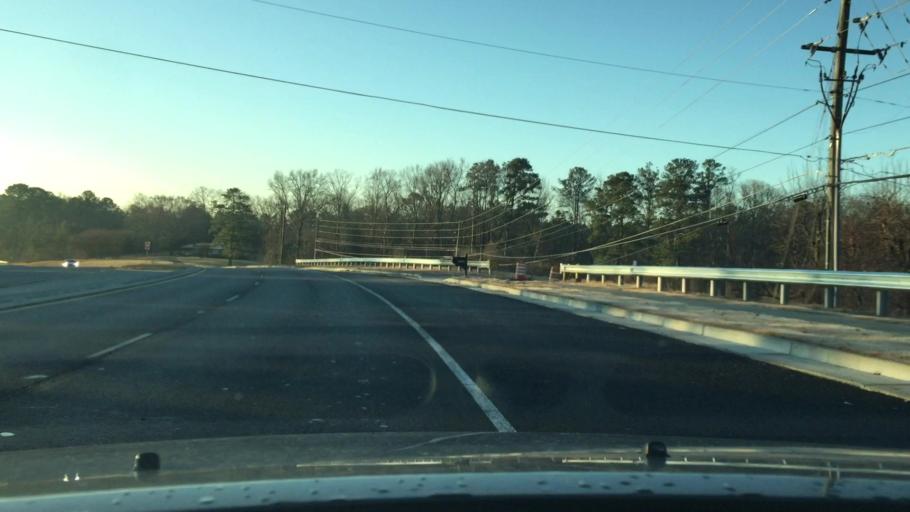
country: US
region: Georgia
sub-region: Forsyth County
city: Cumming
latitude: 34.1883
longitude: -84.1971
